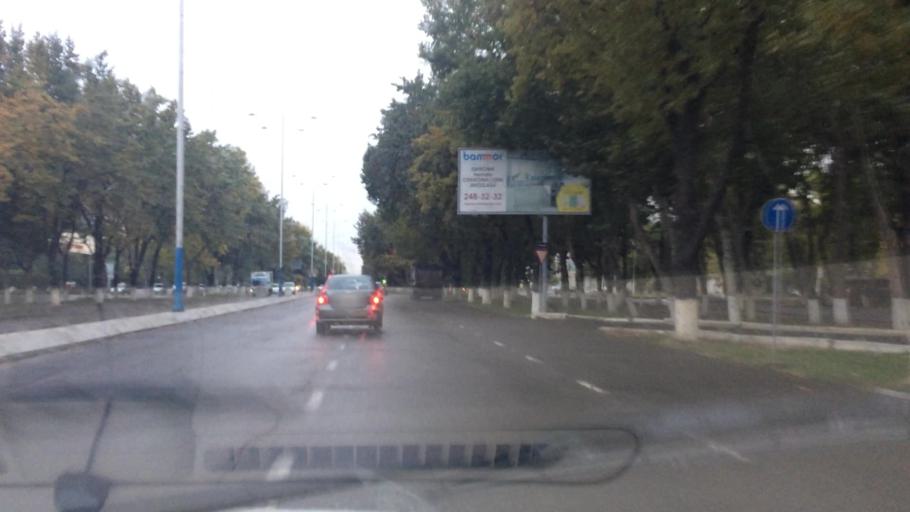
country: UZ
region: Toshkent Shahri
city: Tashkent
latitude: 41.2712
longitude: 69.2024
